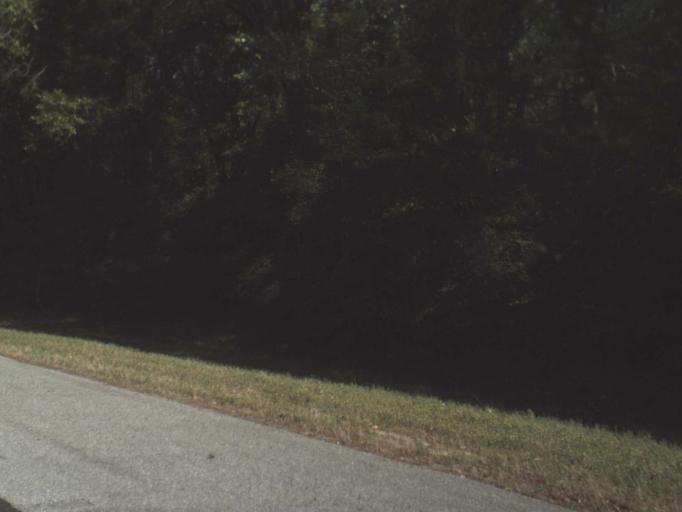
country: US
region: Florida
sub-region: Okaloosa County
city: Crestview
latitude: 30.7077
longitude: -86.7220
